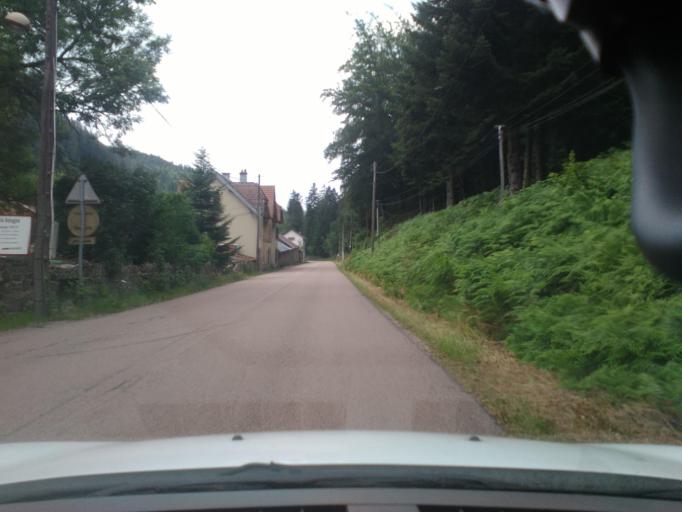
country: FR
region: Lorraine
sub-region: Departement des Vosges
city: Gerardmer
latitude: 48.1016
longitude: 6.8736
